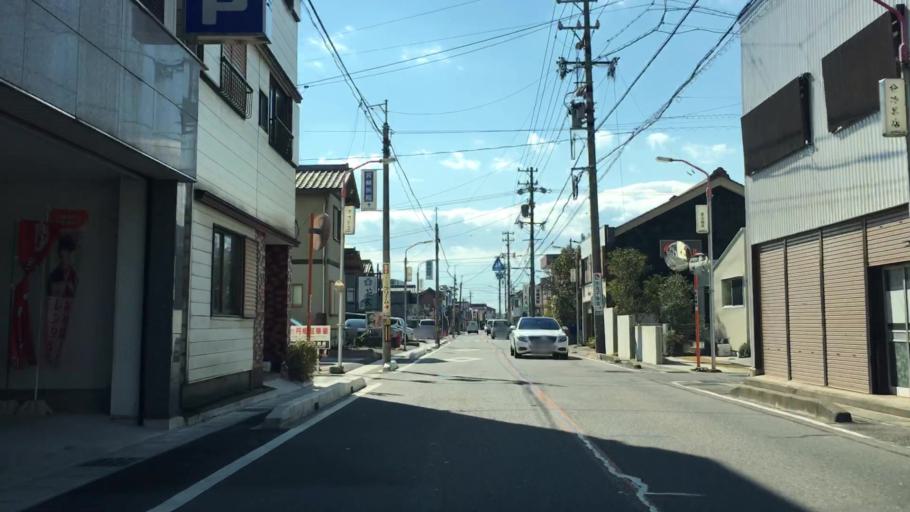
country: JP
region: Aichi
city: Ishiki
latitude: 34.7956
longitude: 137.0721
